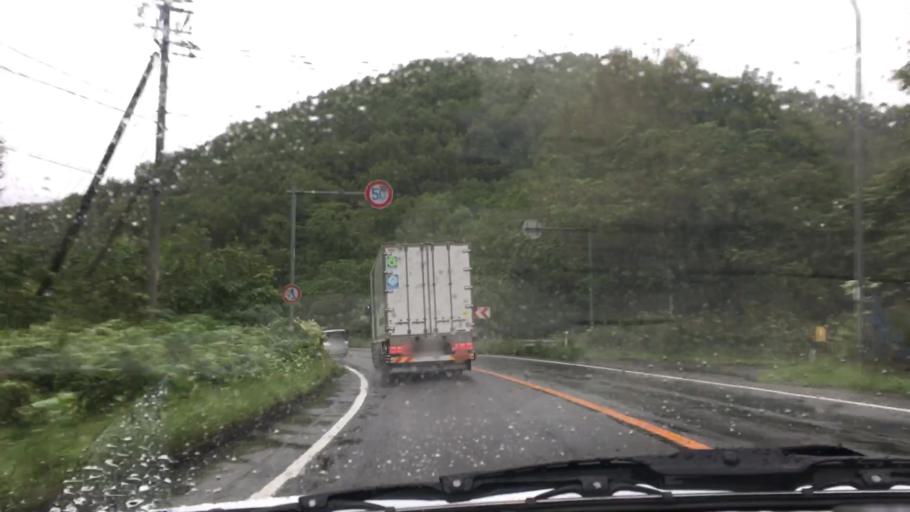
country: JP
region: Hokkaido
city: Niseko Town
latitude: 42.5976
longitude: 140.6729
